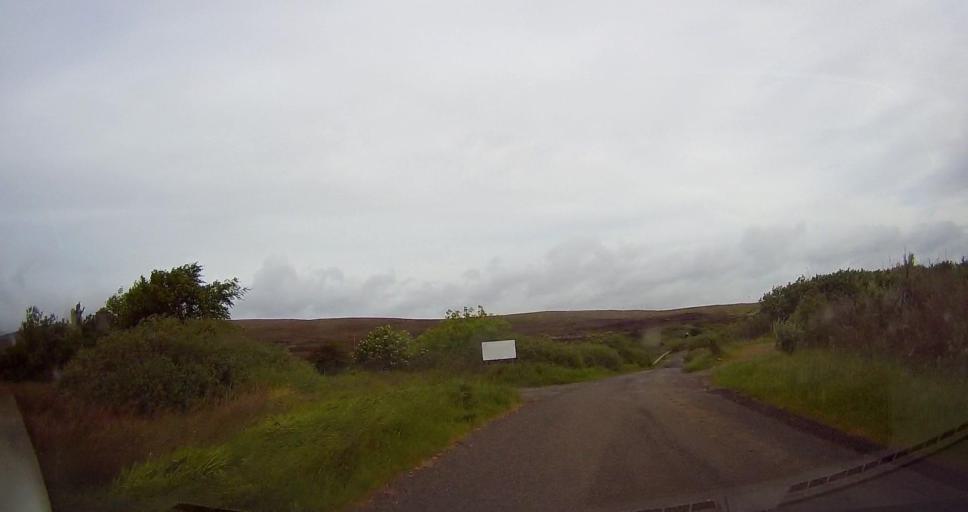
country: GB
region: Scotland
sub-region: Orkney Islands
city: Stromness
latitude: 58.8392
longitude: -3.2169
